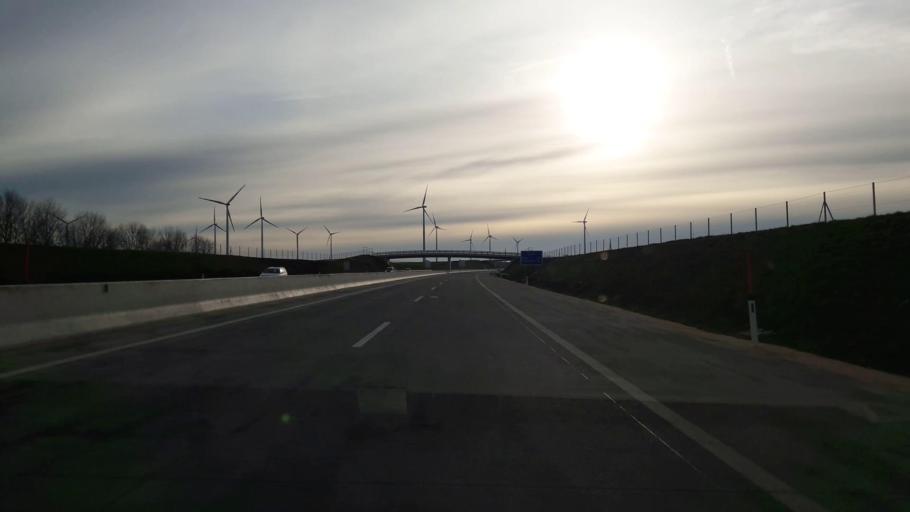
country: AT
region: Lower Austria
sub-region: Politischer Bezirk Mistelbach
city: Grosskrut
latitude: 48.6458
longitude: 16.6885
